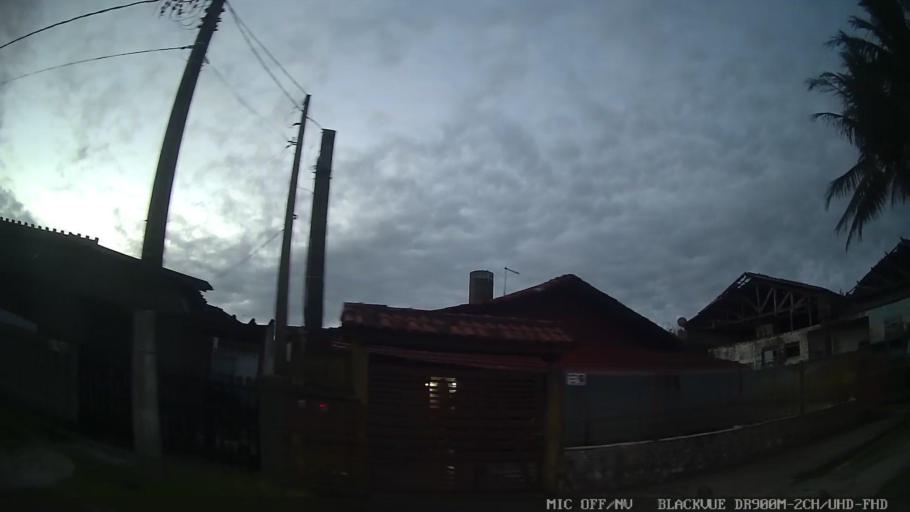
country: BR
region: Sao Paulo
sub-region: Itanhaem
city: Itanhaem
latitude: -24.2460
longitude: -46.8895
